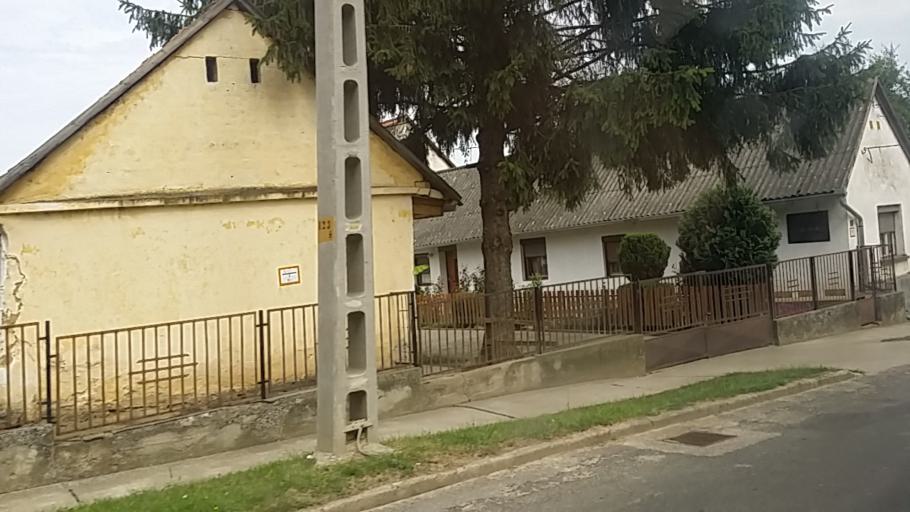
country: HU
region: Baranya
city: Villany
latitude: 45.9074
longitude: 18.4706
